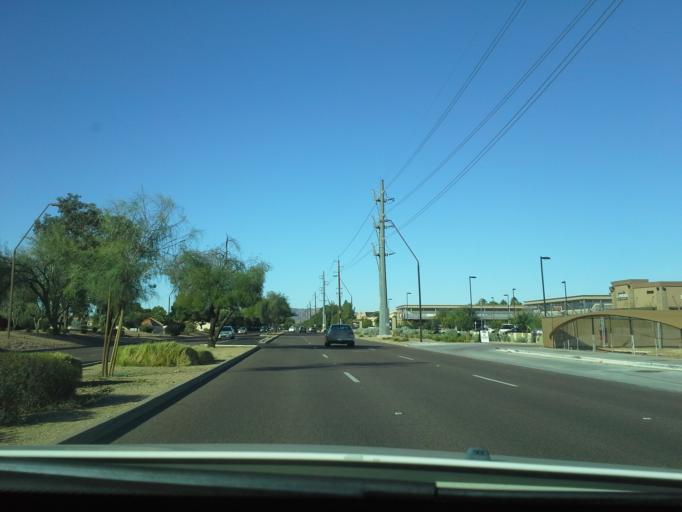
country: US
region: Arizona
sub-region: Maricopa County
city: San Carlos
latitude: 33.3493
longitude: -111.9001
